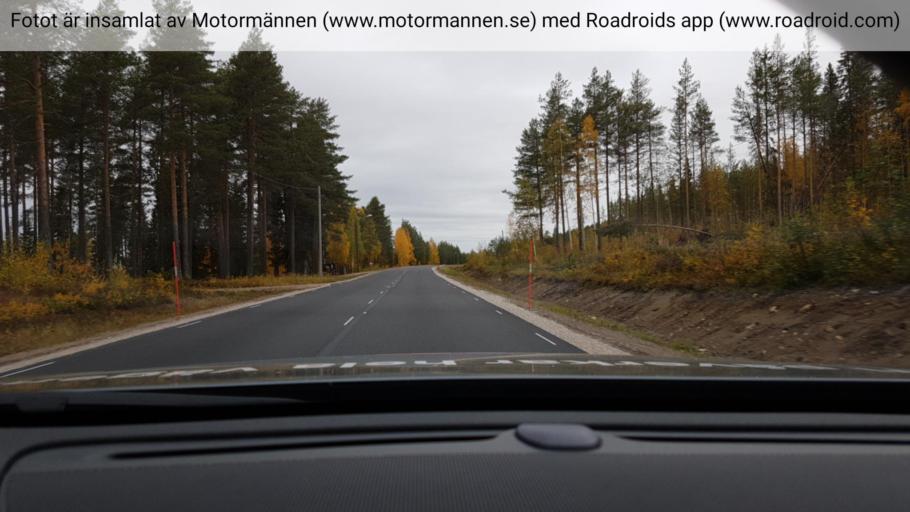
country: SE
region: Norrbotten
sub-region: Overkalix Kommun
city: OEverkalix
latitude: 66.3883
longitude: 22.8230
